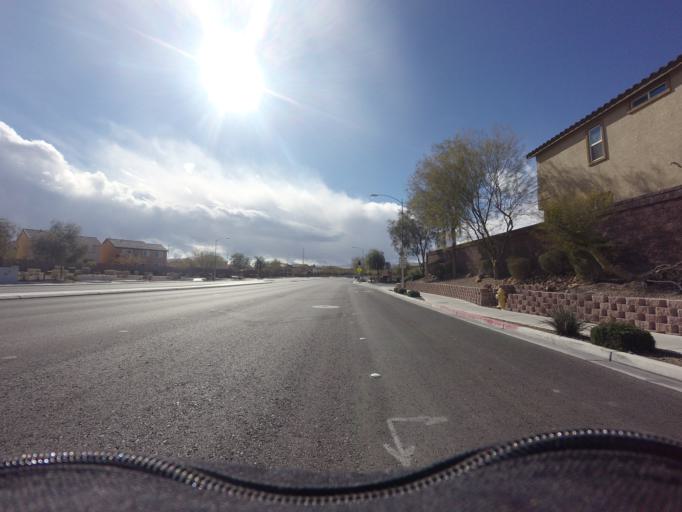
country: US
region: Nevada
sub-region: Clark County
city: Nellis Air Force Base
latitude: 36.2624
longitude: -115.1182
